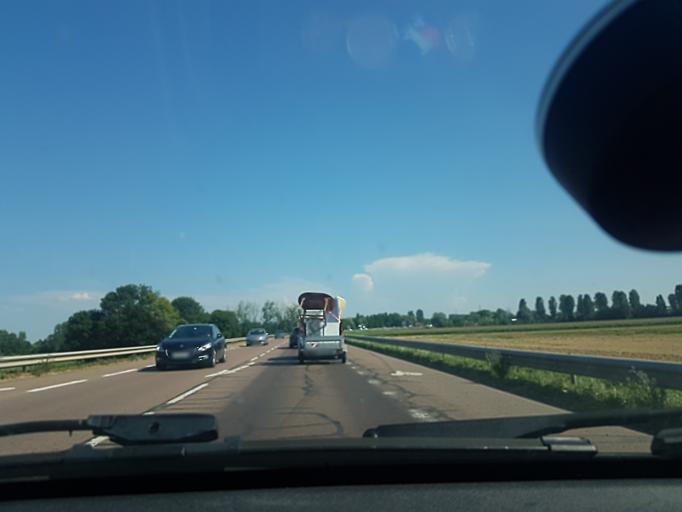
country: FR
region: Bourgogne
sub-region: Departement de Saone-et-Loire
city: Saint-Marcel
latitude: 46.7822
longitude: 4.8734
